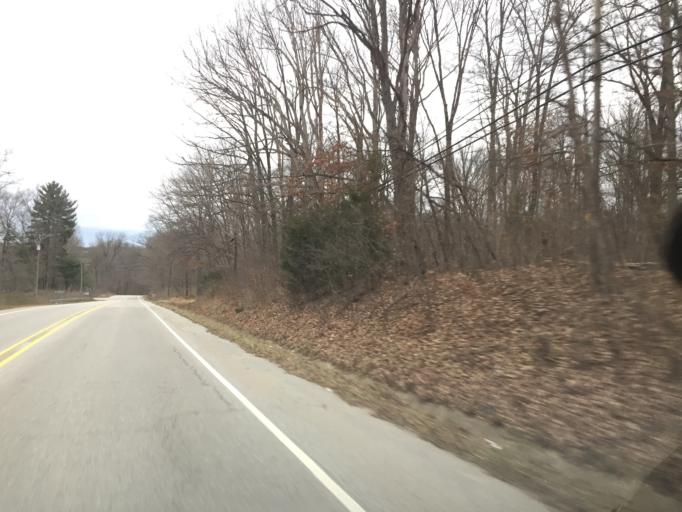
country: US
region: Indiana
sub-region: Monroe County
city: Bloomington
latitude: 39.1963
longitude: -86.5569
